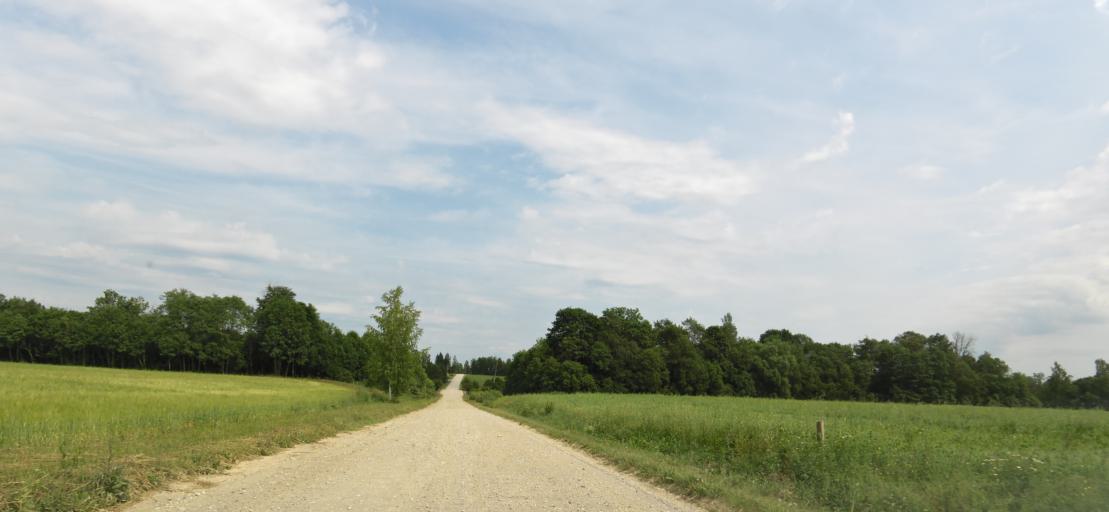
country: LT
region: Panevezys
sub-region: Birzai
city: Birzai
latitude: 56.3754
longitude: 24.7679
